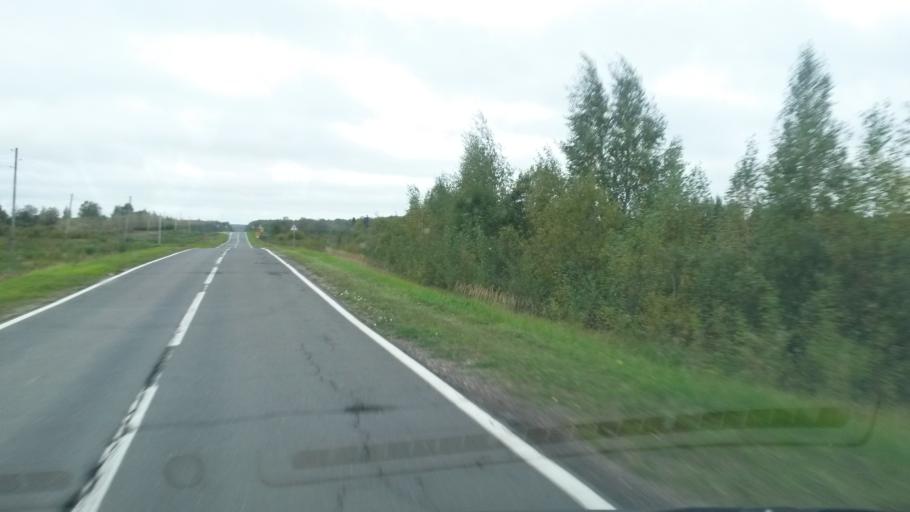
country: RU
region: Jaroslavl
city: Tutayev
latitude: 57.9507
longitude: 39.4353
